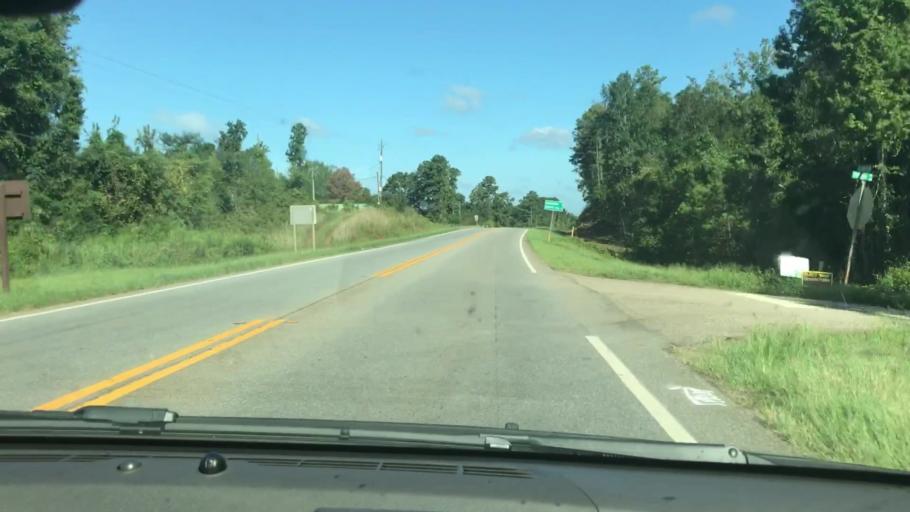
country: US
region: Georgia
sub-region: Quitman County
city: Georgetown
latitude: 31.8610
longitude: -85.0692
